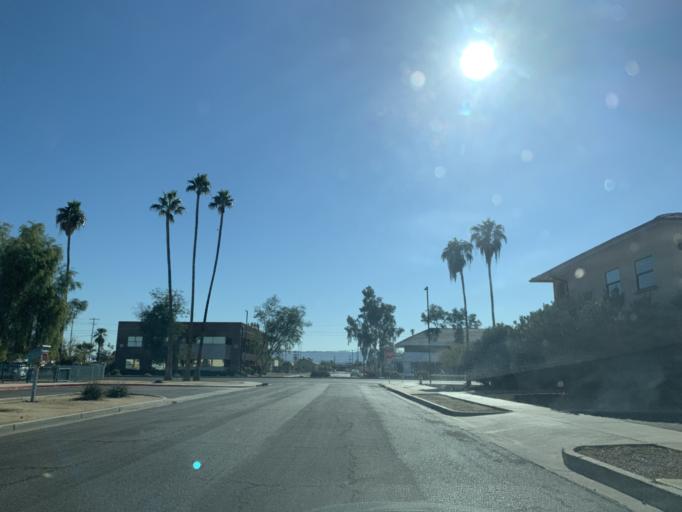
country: US
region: Arizona
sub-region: Maricopa County
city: Phoenix
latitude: 33.4489
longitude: -112.0542
